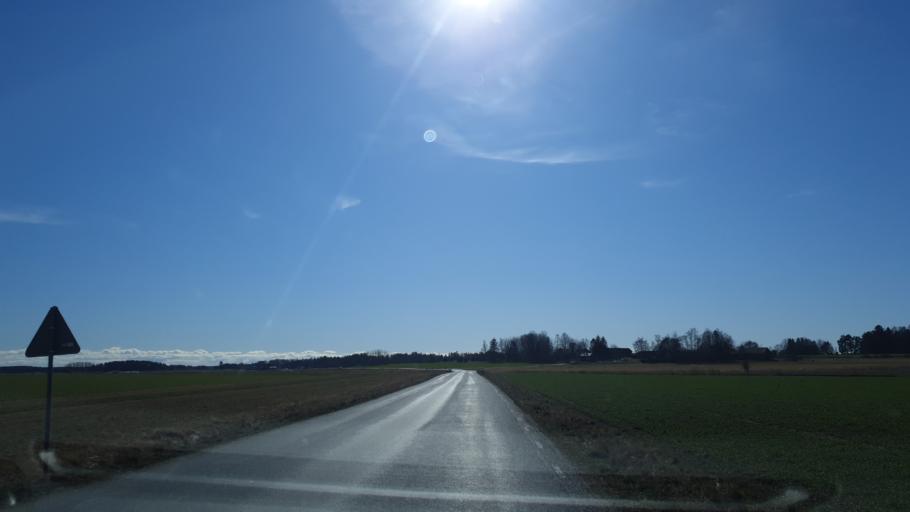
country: SE
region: Uppsala
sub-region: Enkopings Kommun
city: Grillby
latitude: 59.6015
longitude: 17.2728
